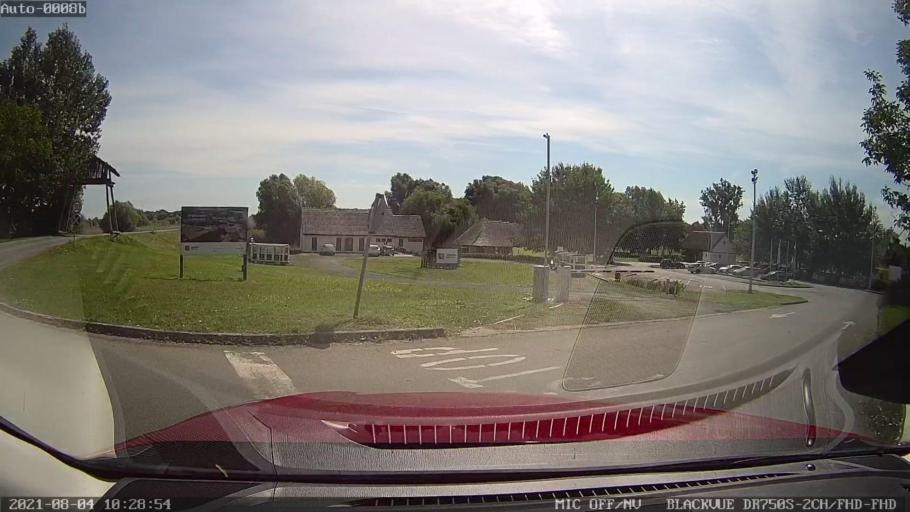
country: HR
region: Osjecko-Baranjska
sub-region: Grad Osijek
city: Bilje
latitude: 45.6082
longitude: 18.7880
